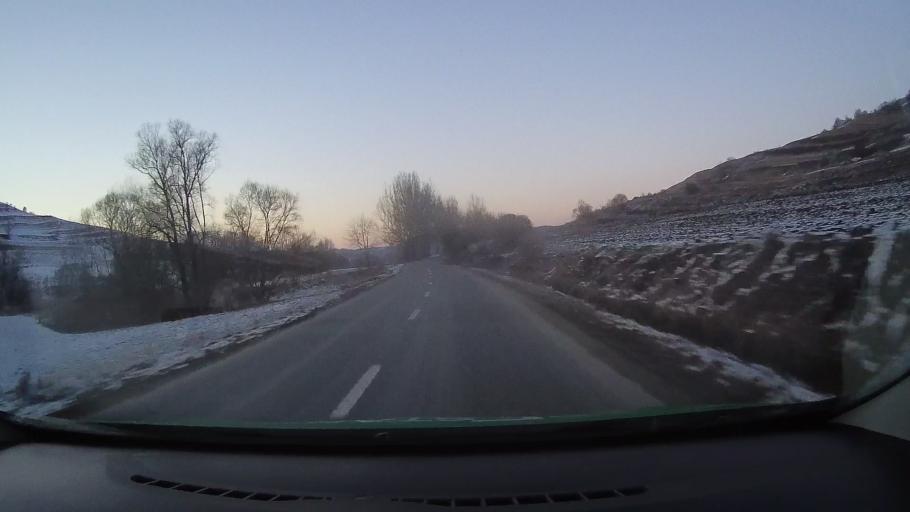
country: RO
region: Sibiu
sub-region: Comuna Alma
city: Alma
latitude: 46.1838
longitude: 24.4722
